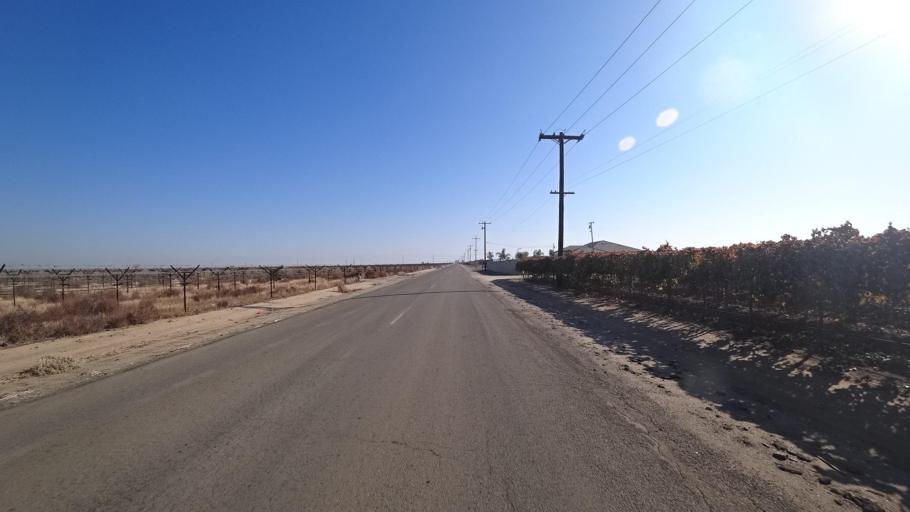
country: US
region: California
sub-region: Kern County
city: Delano
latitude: 35.7469
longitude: -119.2124
